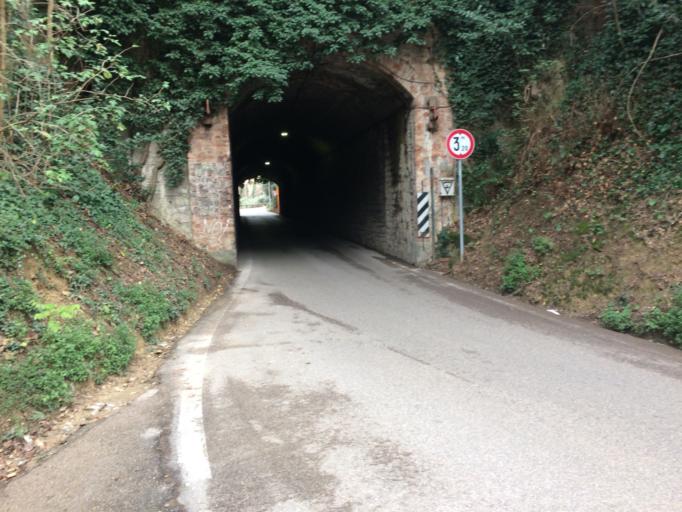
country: IT
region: Umbria
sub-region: Provincia di Perugia
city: Perugia
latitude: 43.1037
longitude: 12.3966
